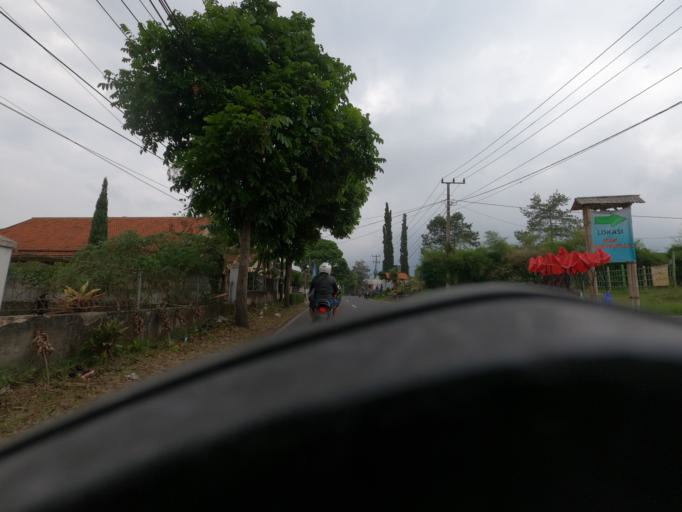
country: ID
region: West Java
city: Lembang
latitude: -6.8103
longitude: 107.5674
